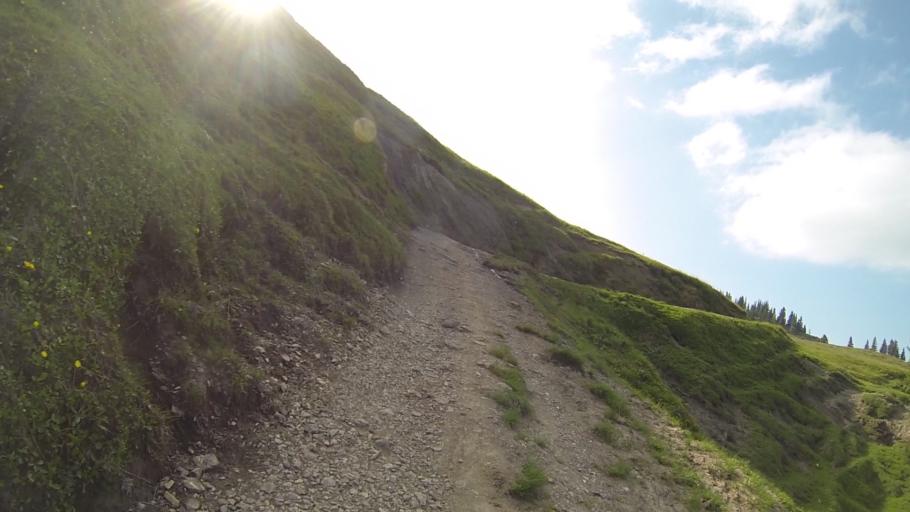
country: DE
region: Bavaria
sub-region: Swabia
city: Nesselwang
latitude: 47.5941
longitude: 10.4979
